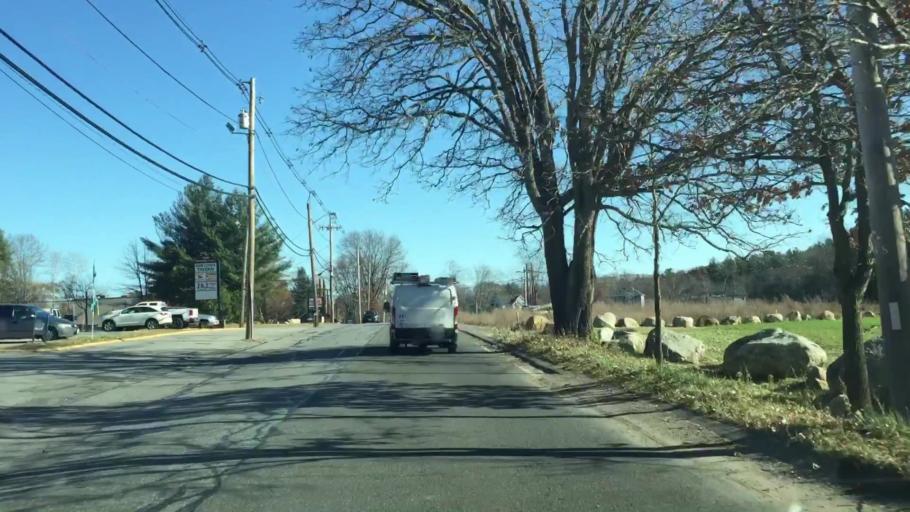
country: US
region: Massachusetts
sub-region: Middlesex County
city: Dracut
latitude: 42.7014
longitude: -71.2514
